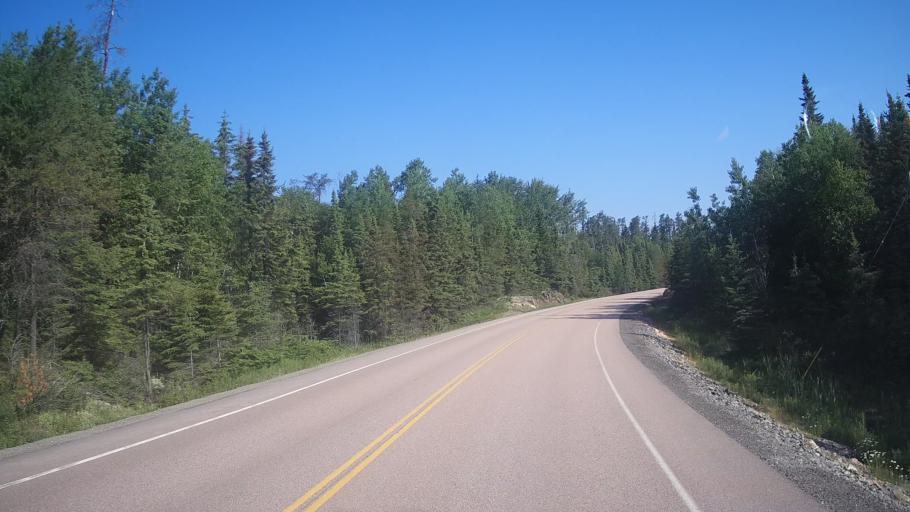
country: CA
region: Ontario
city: Rayside-Balfour
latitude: 46.9815
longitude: -81.6341
